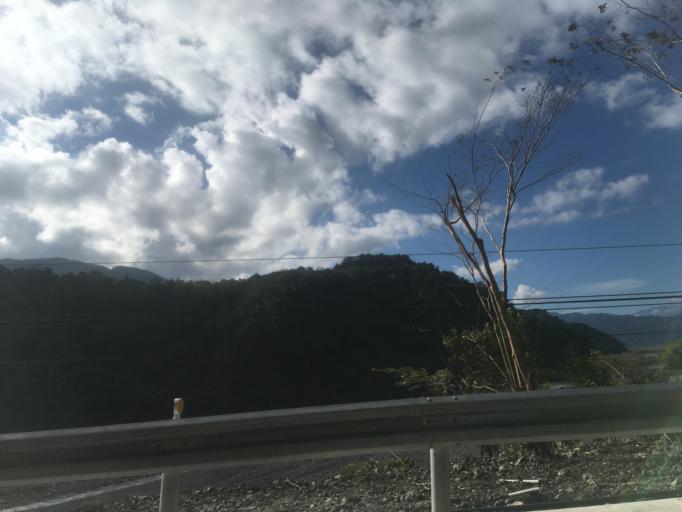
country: TW
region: Taiwan
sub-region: Yilan
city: Yilan
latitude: 24.6415
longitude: 121.5620
